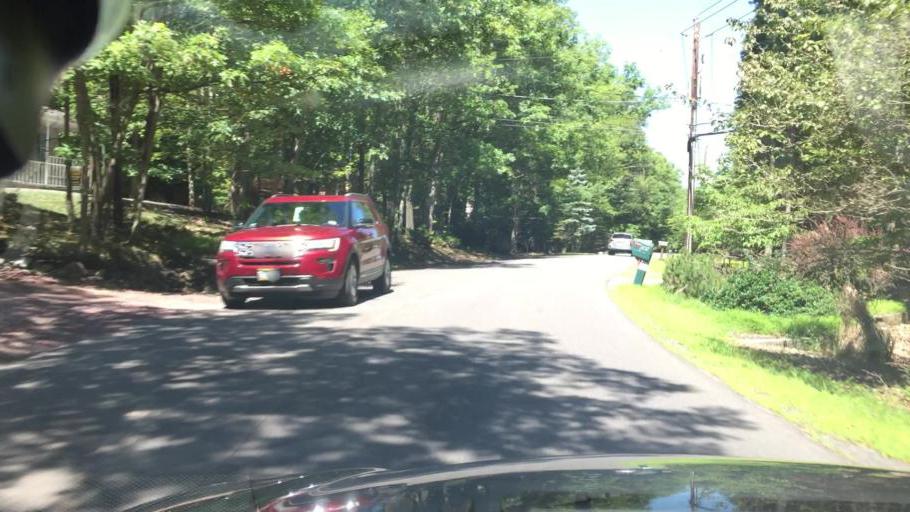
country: US
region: Pennsylvania
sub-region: Luzerne County
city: Freeland
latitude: 41.0401
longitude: -75.9376
